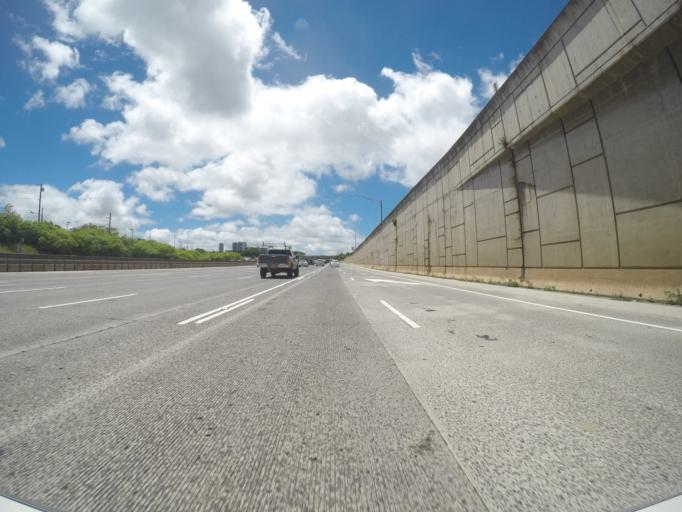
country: US
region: Hawaii
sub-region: Honolulu County
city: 'Aiea
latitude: 21.3802
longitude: -157.9291
